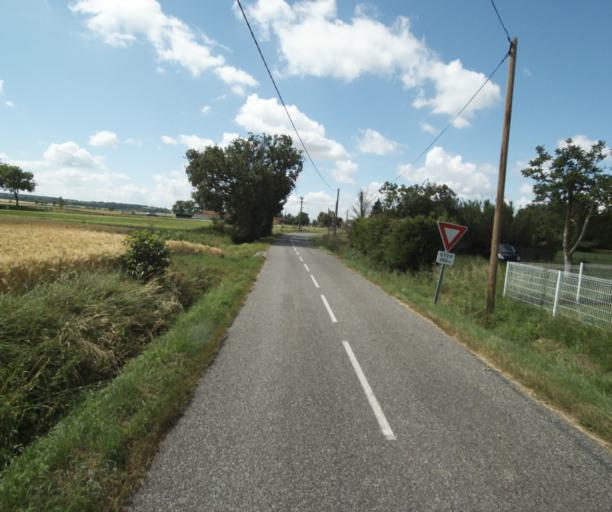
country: FR
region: Midi-Pyrenees
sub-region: Departement de la Haute-Garonne
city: Saint-Felix-Lauragais
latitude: 43.4503
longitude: 1.9172
